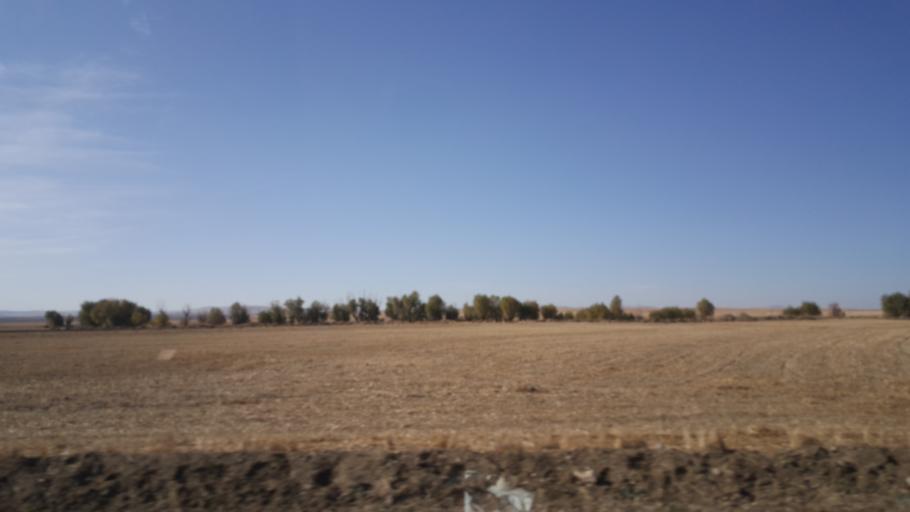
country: TR
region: Ankara
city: Yenice
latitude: 39.3766
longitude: 32.8154
